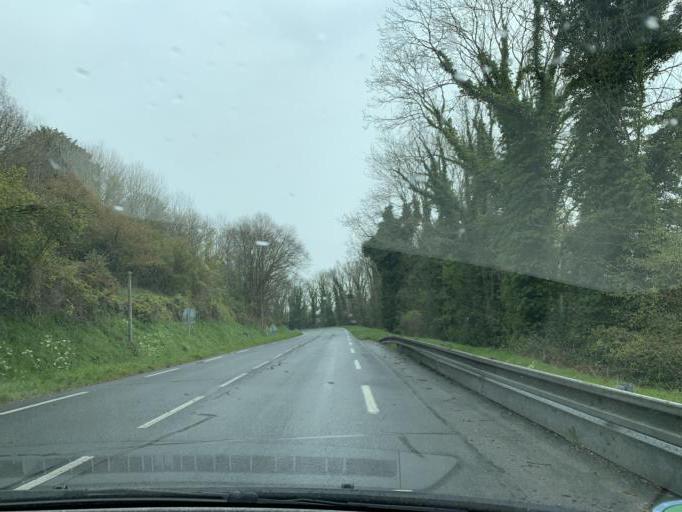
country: FR
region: Haute-Normandie
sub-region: Departement de la Seine-Maritime
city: Fecamp
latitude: 49.7629
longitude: 0.3965
